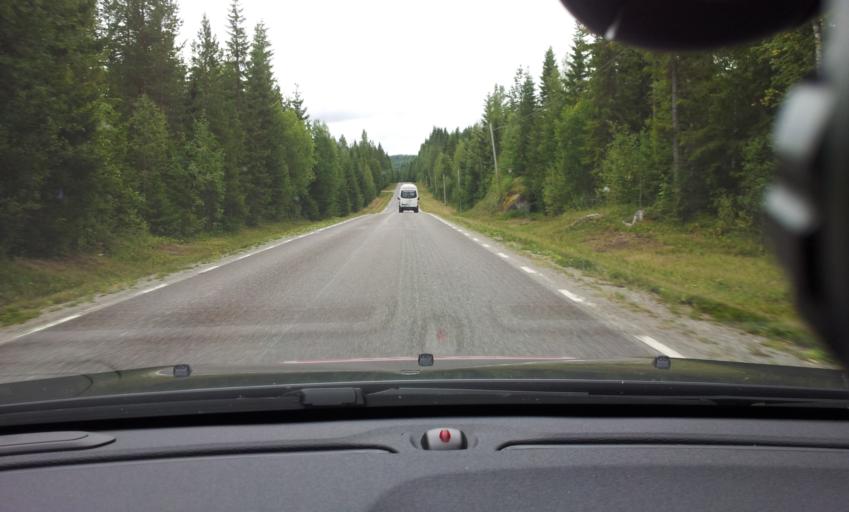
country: SE
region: Jaemtland
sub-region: Braecke Kommun
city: Braecke
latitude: 63.0111
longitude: 15.1991
